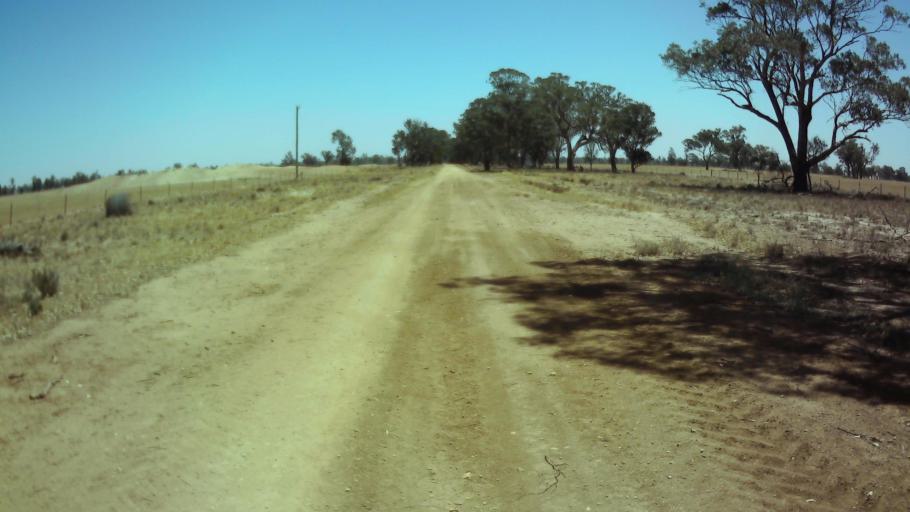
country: AU
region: New South Wales
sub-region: Weddin
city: Grenfell
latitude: -34.0329
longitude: 147.8637
